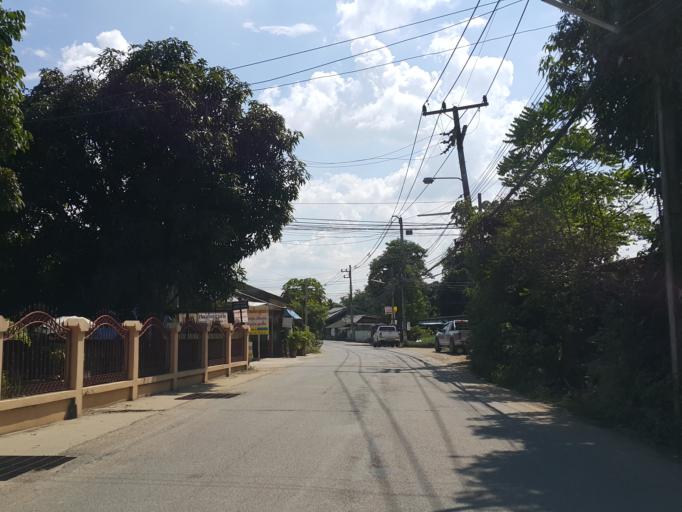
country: TH
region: Chiang Mai
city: Saraphi
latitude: 18.7594
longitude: 99.0539
